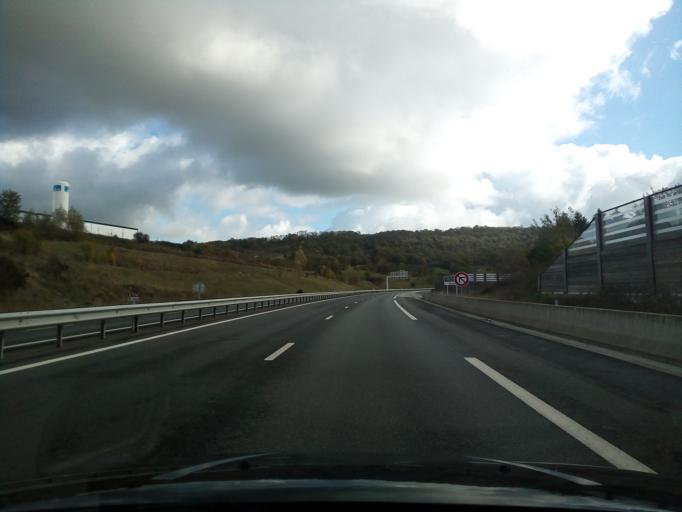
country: FR
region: Auvergne
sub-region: Departement de l'Allier
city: Saint-Victor
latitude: 46.3804
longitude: 2.6194
